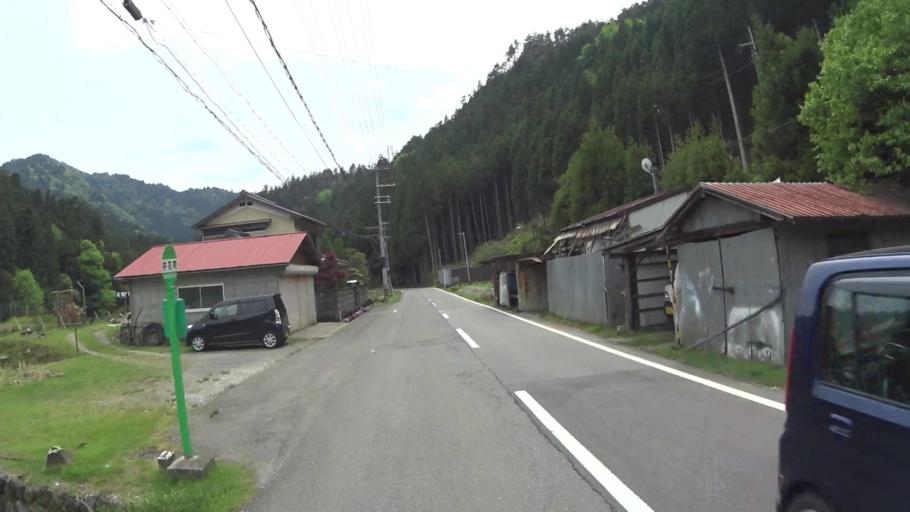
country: JP
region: Kyoto
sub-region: Kyoto-shi
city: Kamigyo-ku
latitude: 35.2017
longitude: 135.7108
